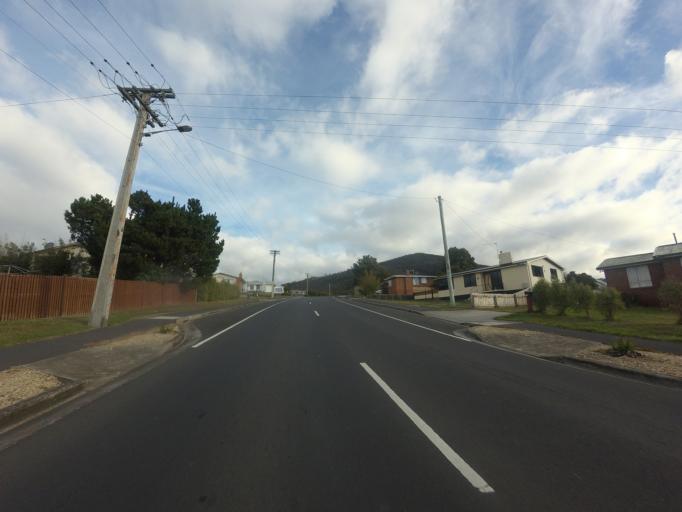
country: AU
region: Tasmania
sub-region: Glenorchy
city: Berriedale
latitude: -42.8125
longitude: 147.2418
